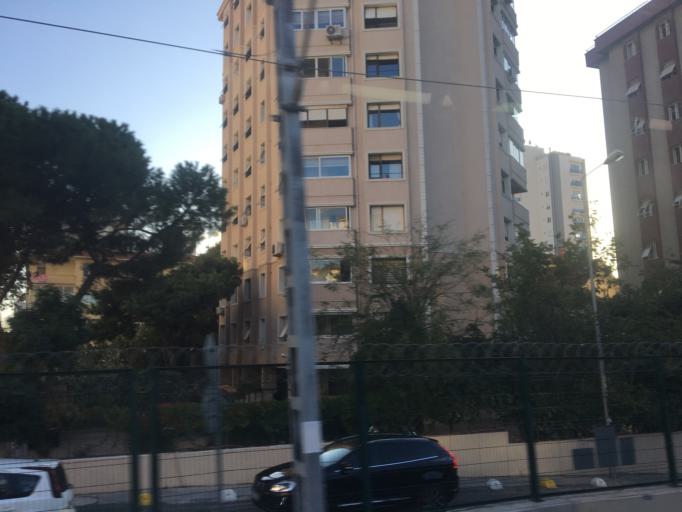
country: TR
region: Istanbul
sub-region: Atasehir
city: Atasehir
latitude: 40.9760
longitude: 29.0714
